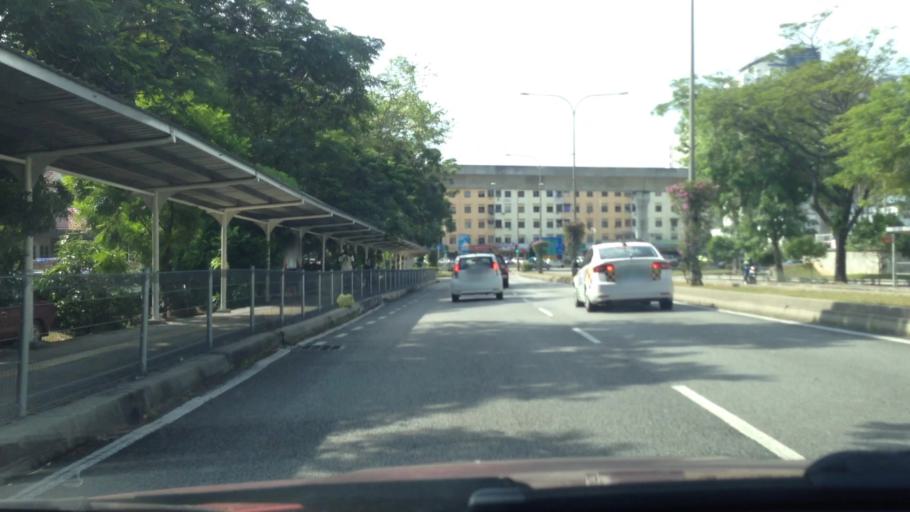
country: MY
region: Selangor
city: Subang Jaya
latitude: 3.0476
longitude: 101.5882
